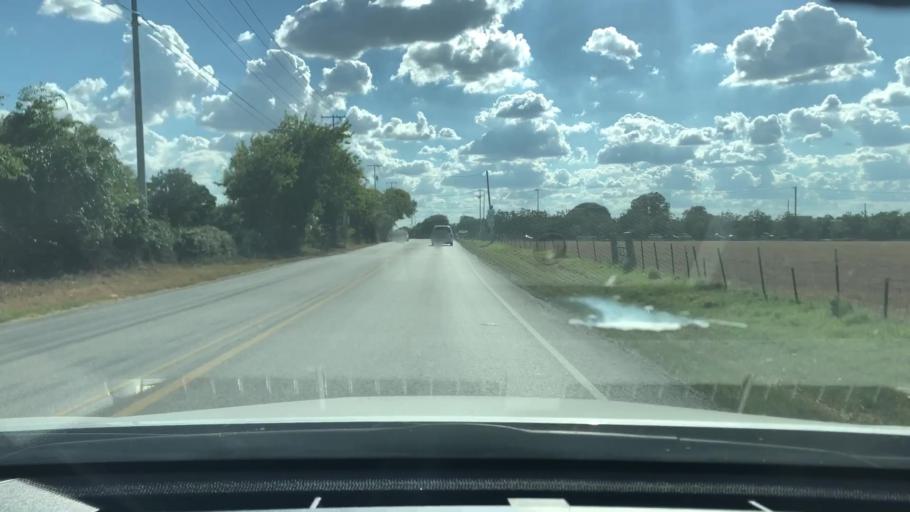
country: US
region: Texas
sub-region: Guadalupe County
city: Northcliff
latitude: 29.6451
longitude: -98.2242
